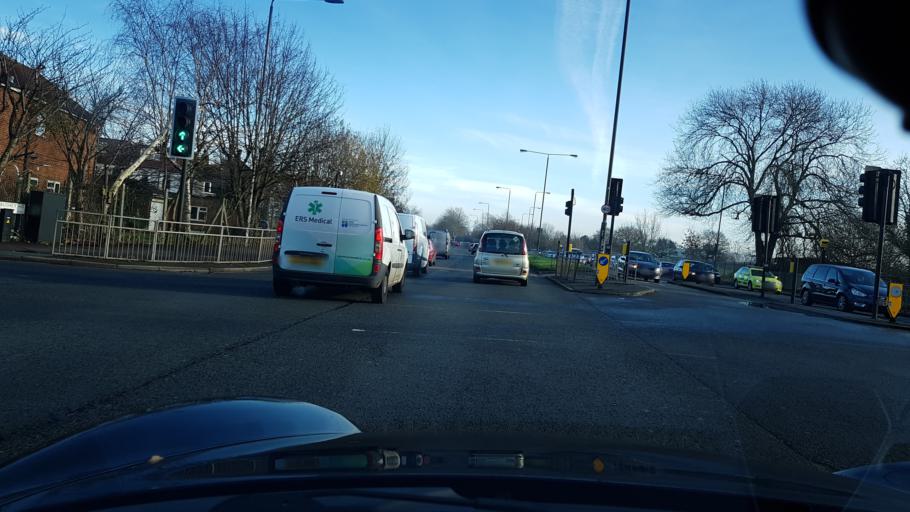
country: GB
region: England
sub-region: Greater London
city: New Malden
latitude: 51.4072
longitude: -0.2298
